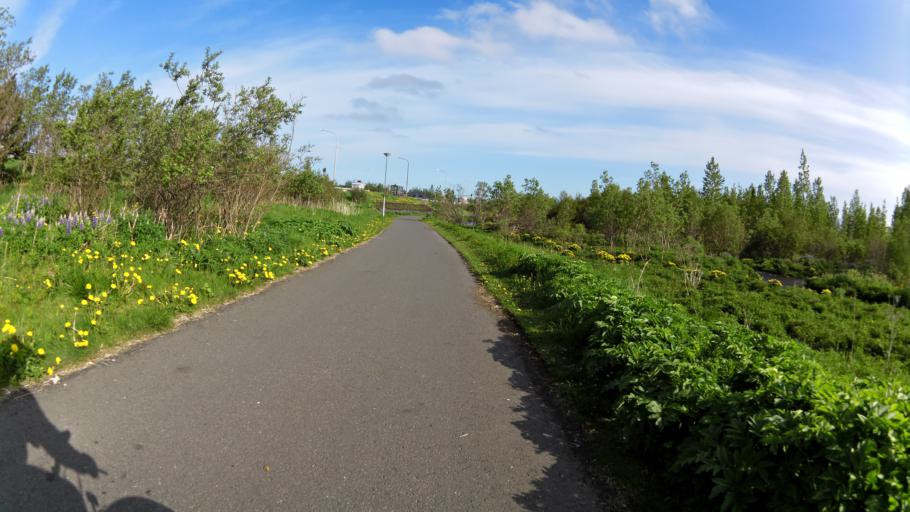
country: IS
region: Capital Region
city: Reykjavik
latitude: 64.1182
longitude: -21.8440
